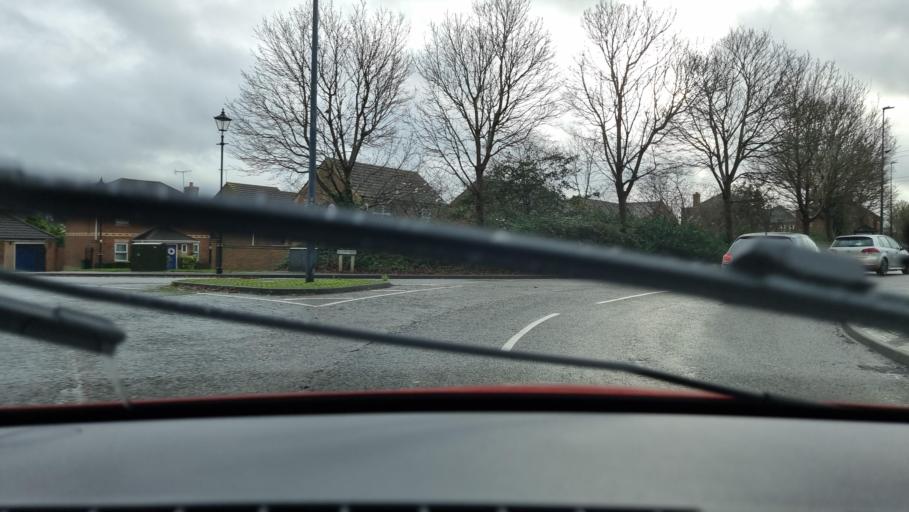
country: GB
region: England
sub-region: Buckinghamshire
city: Aylesbury
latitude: 51.8170
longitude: -0.8352
